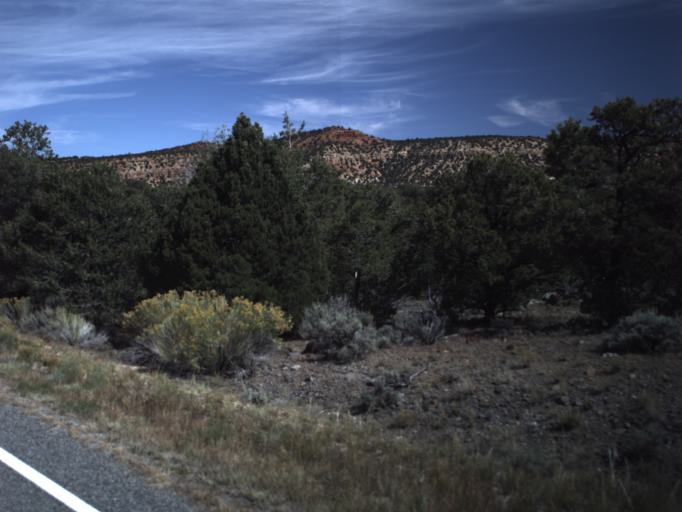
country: US
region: Utah
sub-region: Wayne County
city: Loa
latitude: 38.2169
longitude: -111.3459
